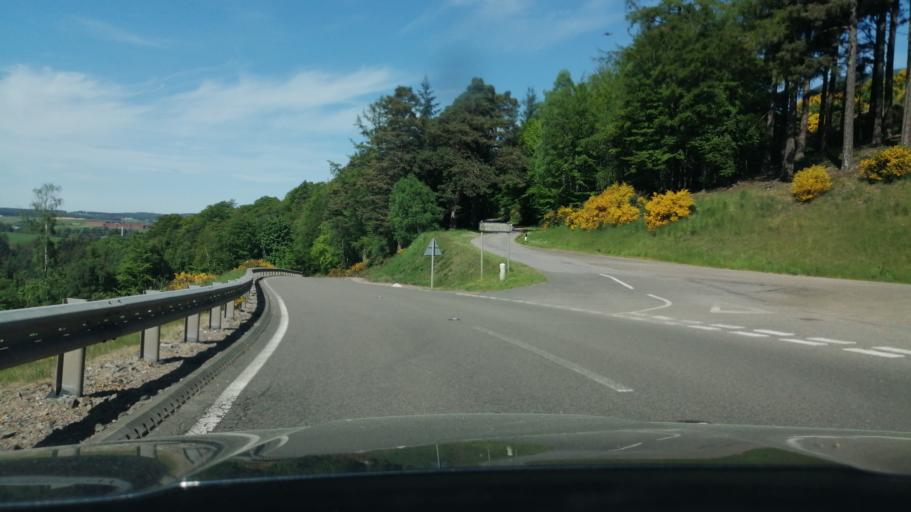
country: GB
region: Scotland
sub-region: Moray
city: Rothes
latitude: 57.4889
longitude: -3.1694
